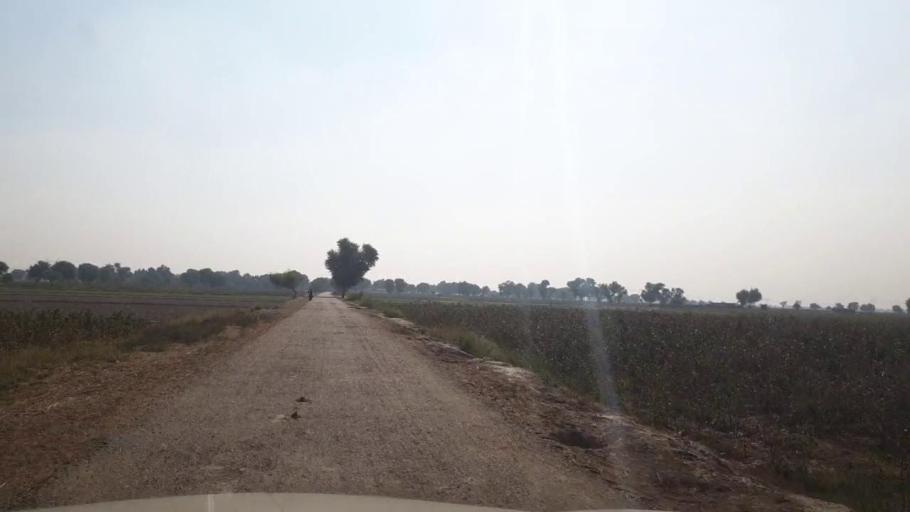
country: PK
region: Sindh
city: Bhan
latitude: 26.5352
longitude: 67.7632
